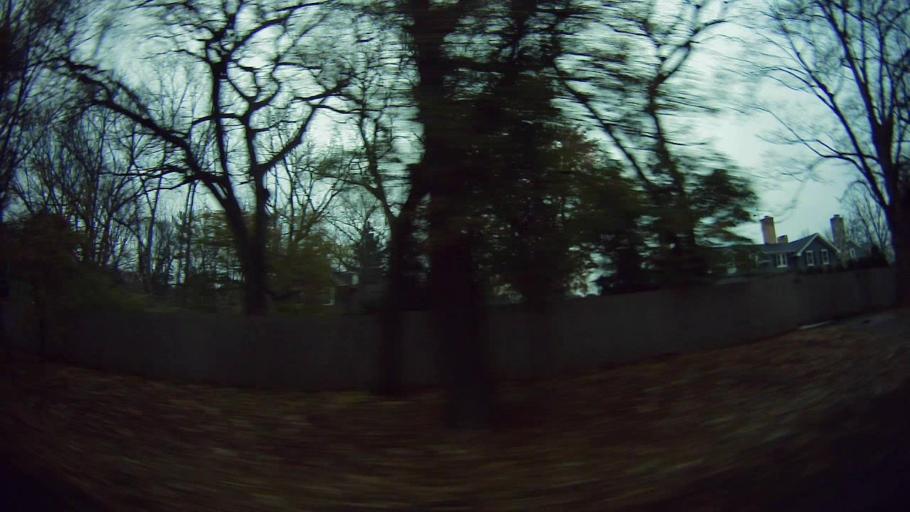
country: US
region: Michigan
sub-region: Oakland County
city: Bingham Farms
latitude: 42.5556
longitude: -83.2802
